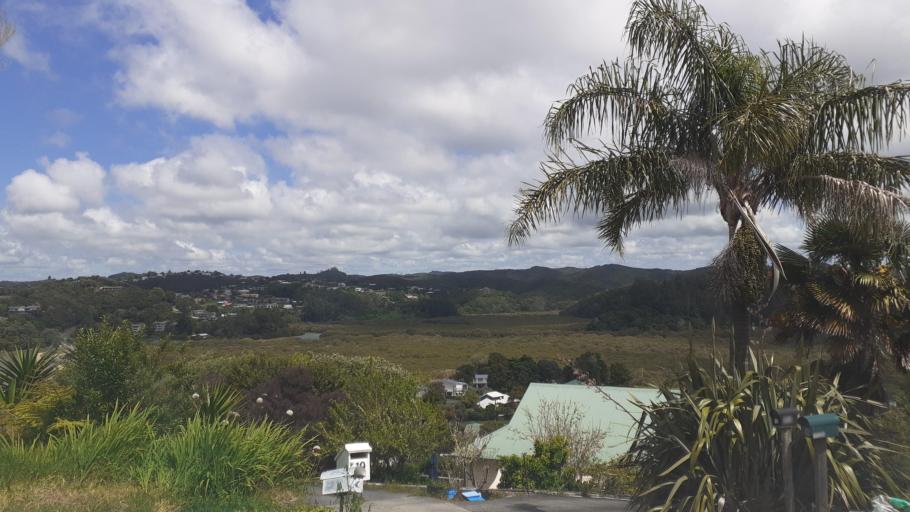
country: NZ
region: Northland
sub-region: Far North District
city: Paihia
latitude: -35.2911
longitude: 174.0987
